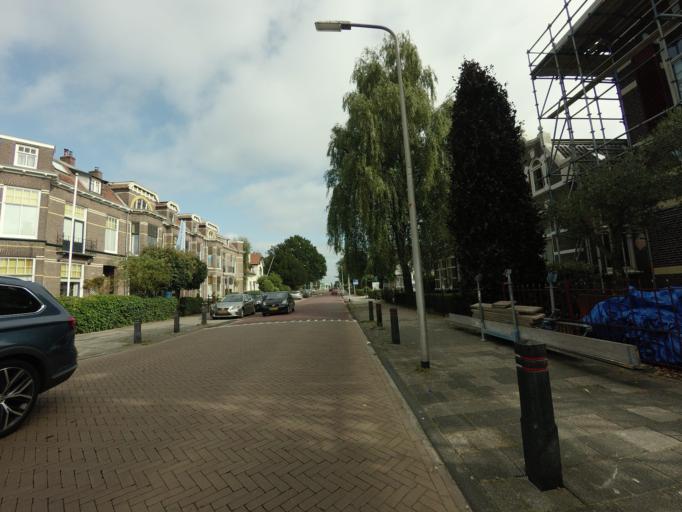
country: NL
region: Overijssel
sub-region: Gemeente Steenwijkerland
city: Steenwijk
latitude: 52.7890
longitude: 6.1208
